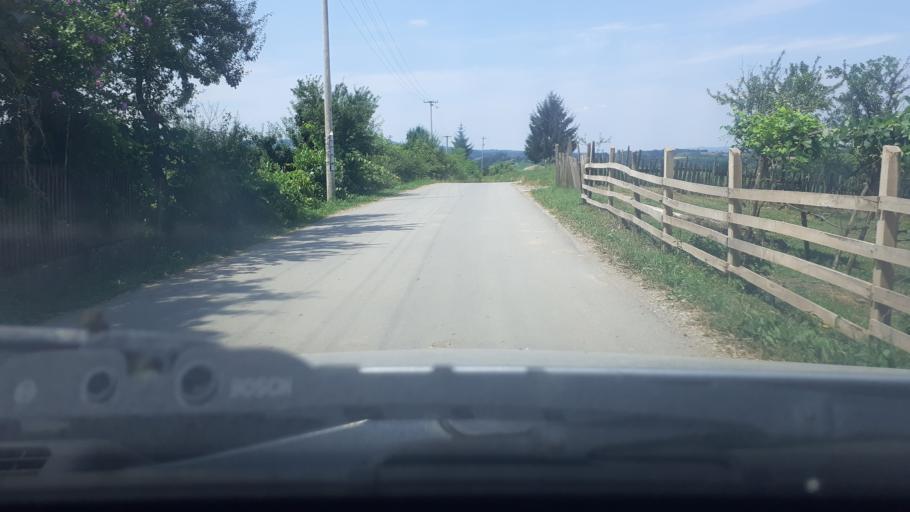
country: RS
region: Central Serbia
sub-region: Kolubarski Okrug
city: Osecina
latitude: 44.3925
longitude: 19.4950
